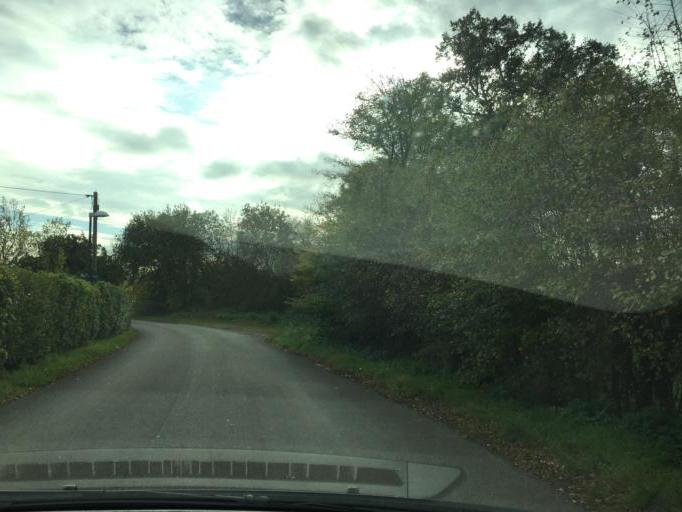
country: DE
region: North Rhine-Westphalia
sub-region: Regierungsbezirk Koln
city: Dueren
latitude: 50.7904
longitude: 6.4778
